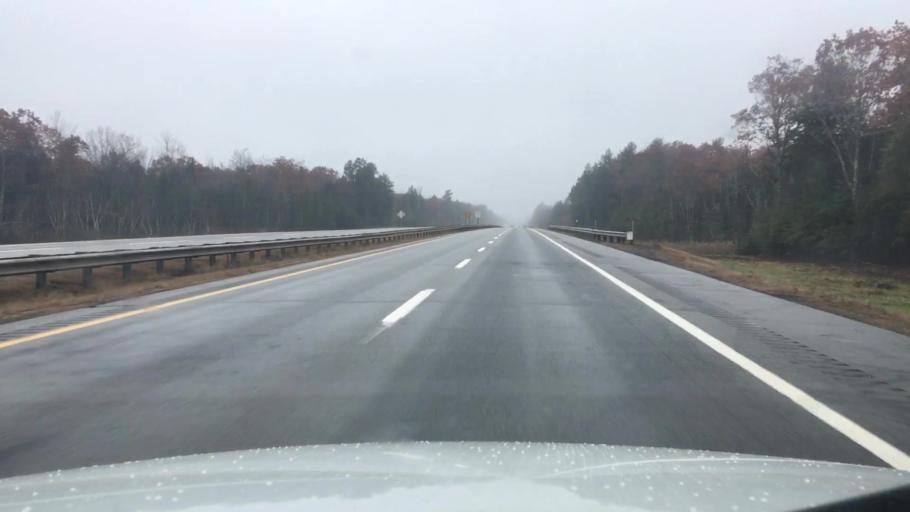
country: US
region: Maine
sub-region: Sagadahoc County
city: Richmond
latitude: 44.1658
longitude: -69.8770
